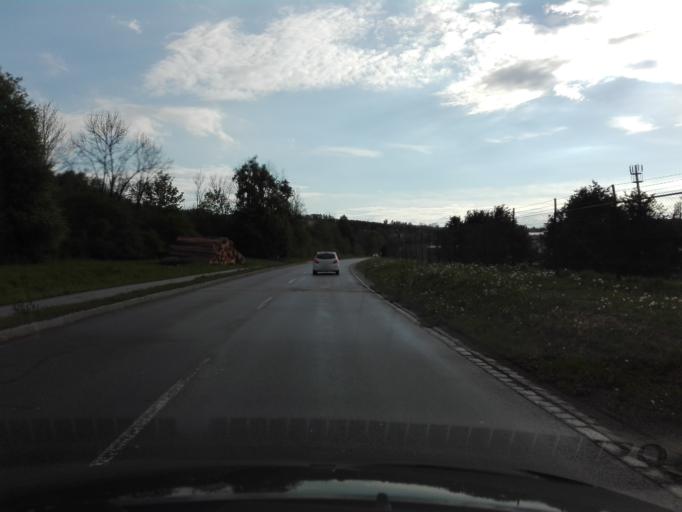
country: DE
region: Bavaria
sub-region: Lower Bavaria
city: Salzweg
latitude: 48.5750
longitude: 13.5003
